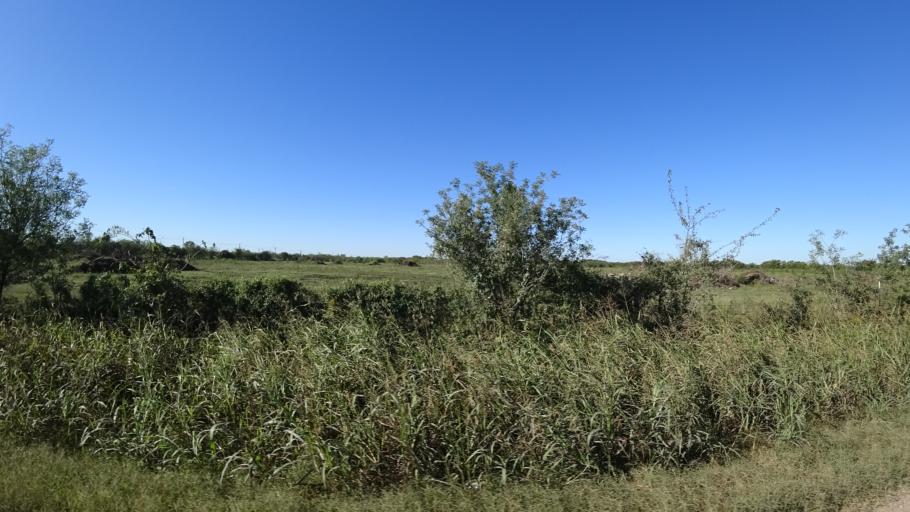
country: US
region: Texas
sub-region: Travis County
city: Hornsby Bend
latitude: 30.2385
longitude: -97.6633
